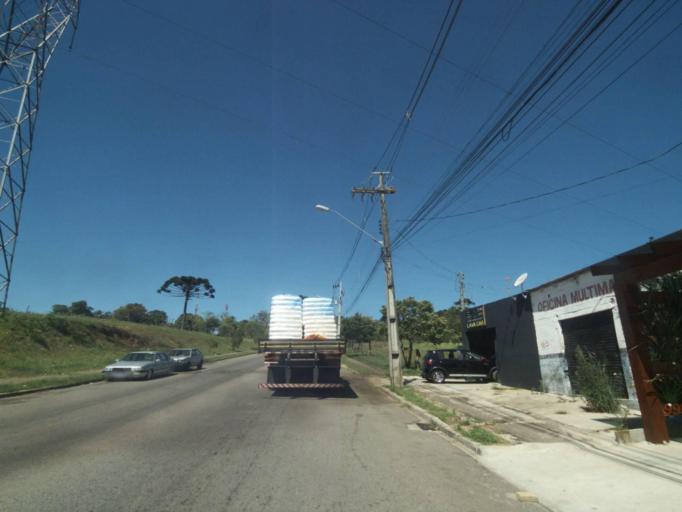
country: BR
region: Parana
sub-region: Curitiba
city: Curitiba
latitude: -25.4646
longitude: -49.3515
